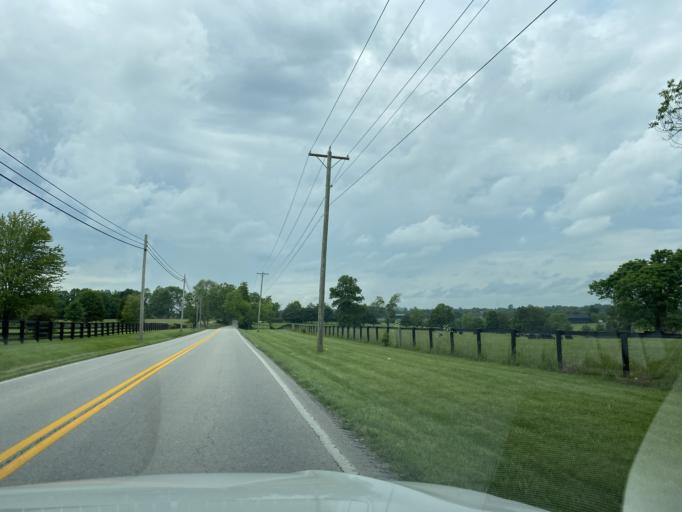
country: US
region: Kentucky
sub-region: Scott County
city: Georgetown
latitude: 38.2191
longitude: -84.4926
